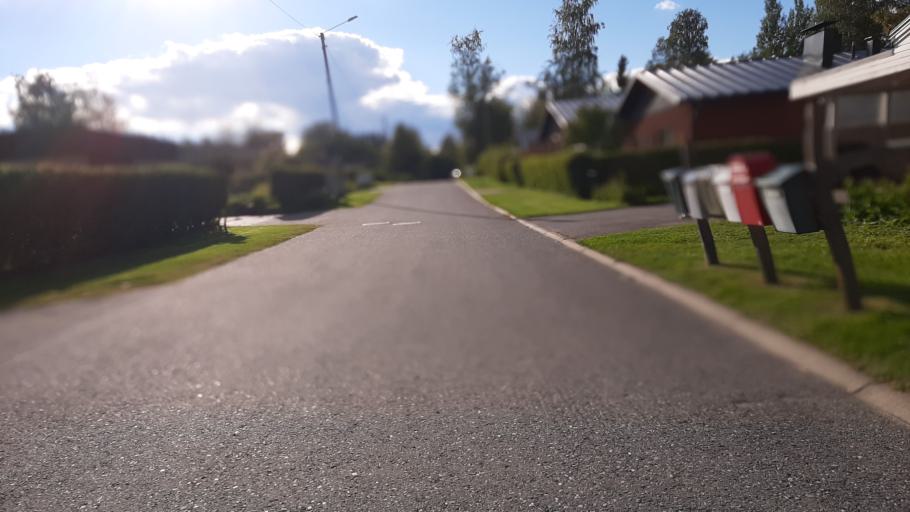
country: FI
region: North Karelia
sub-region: Joensuu
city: Joensuu
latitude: 62.6021
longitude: 29.8100
